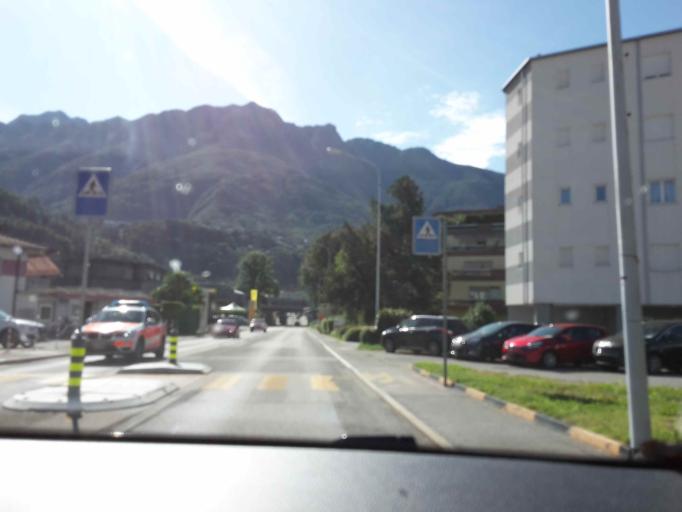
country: CH
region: Ticino
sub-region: Bellinzona District
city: Giubiasco
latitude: 46.1823
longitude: 9.0131
